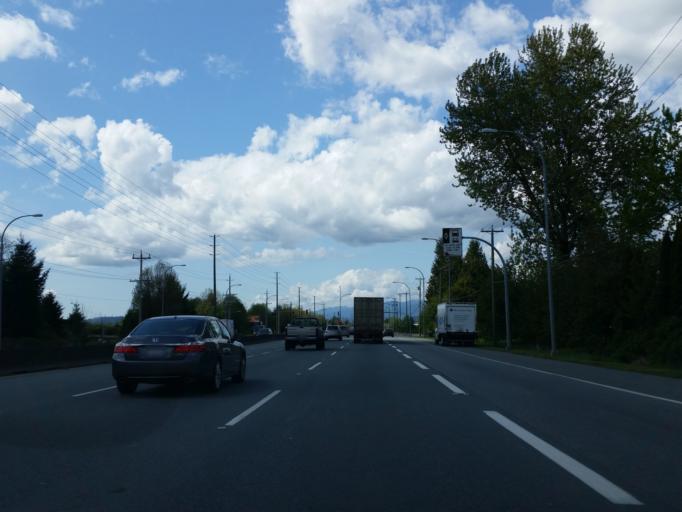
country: CA
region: British Columbia
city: Pitt Meadows
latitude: 49.2343
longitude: -122.6976
